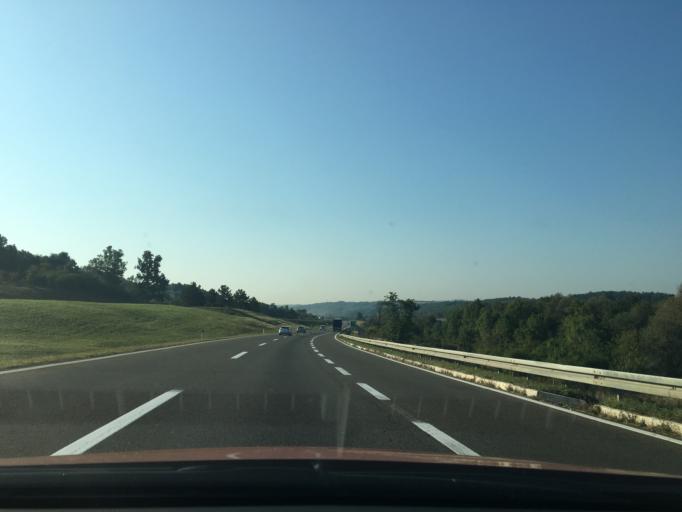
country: RS
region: Central Serbia
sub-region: Belgrade
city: Grocka
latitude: 44.6122
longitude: 20.6416
